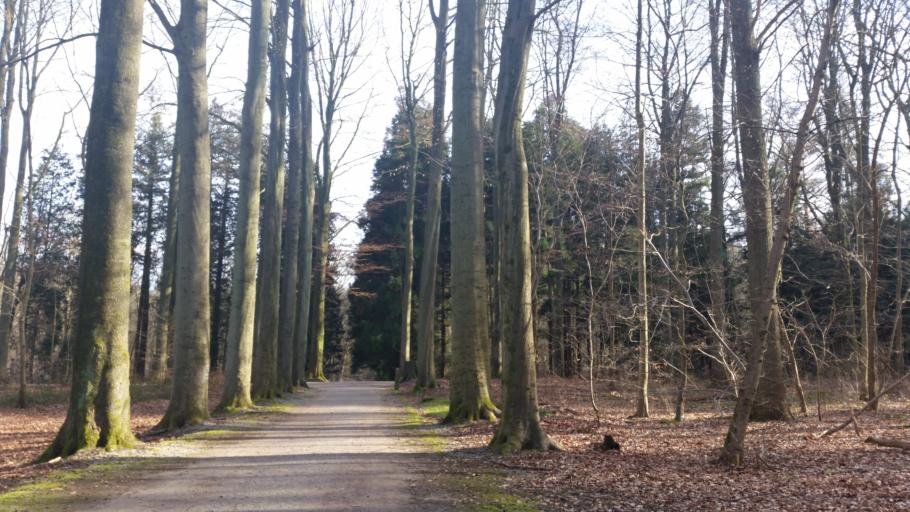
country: BE
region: Flanders
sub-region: Provincie Vlaams-Brabant
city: Tervuren
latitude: 50.8101
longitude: 4.5167
